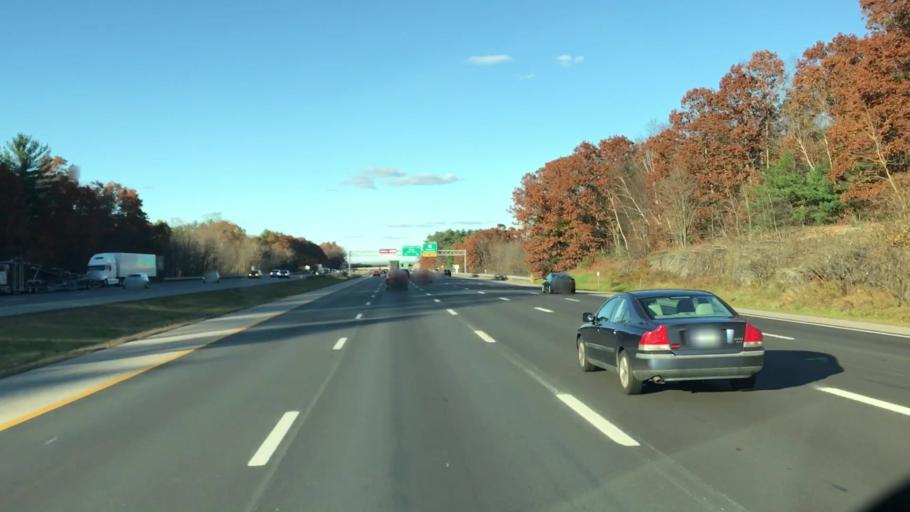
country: US
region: New Hampshire
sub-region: Rockingham County
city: Hampton
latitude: 42.9487
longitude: -70.8590
